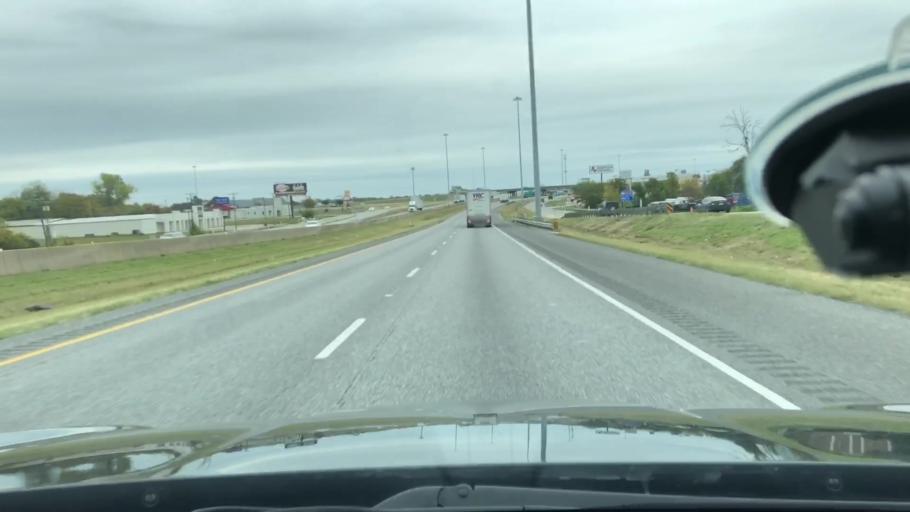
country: US
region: Texas
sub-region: Hunt County
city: Greenville
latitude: 33.1104
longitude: -96.1019
